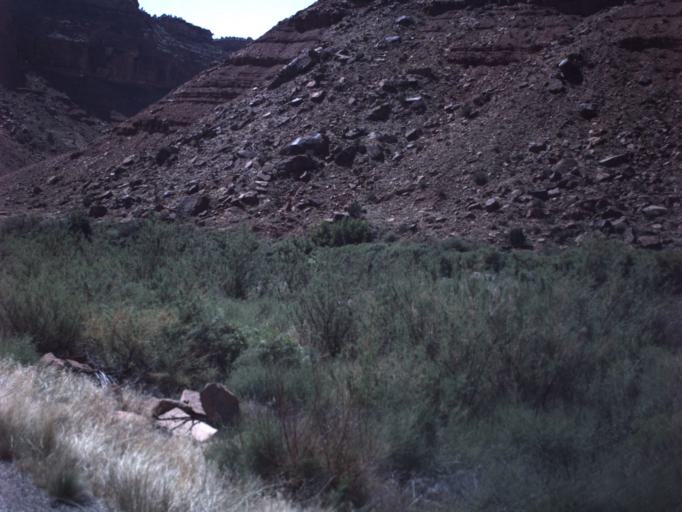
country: US
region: Utah
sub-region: Grand County
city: Moab
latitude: 38.7978
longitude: -109.3403
